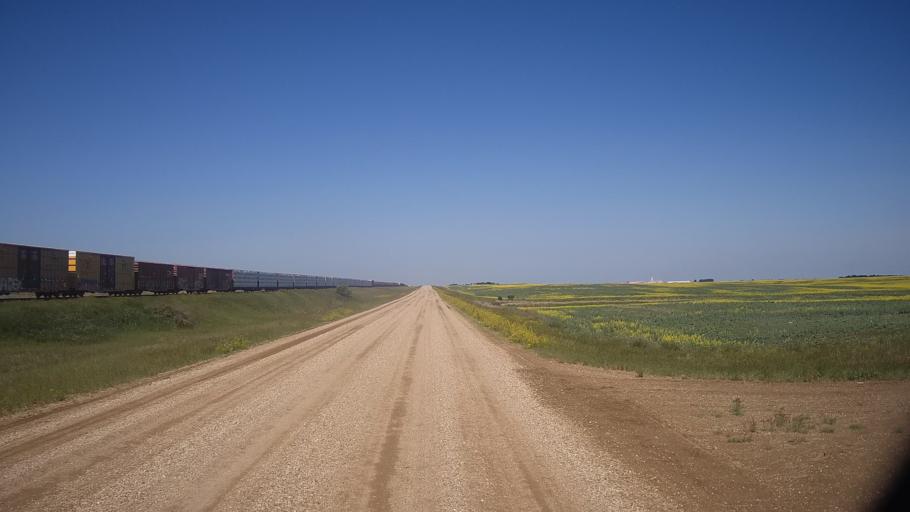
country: CA
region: Saskatchewan
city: Watrous
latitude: 51.8553
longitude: -105.9481
